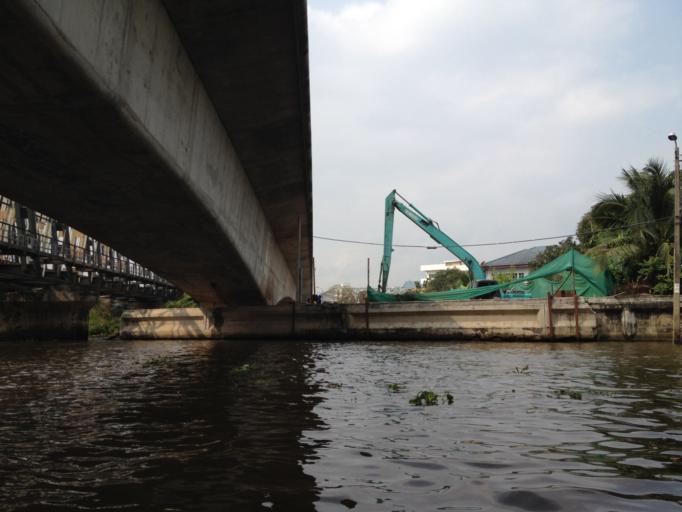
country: TH
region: Bangkok
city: Taling Chan
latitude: 13.7894
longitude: 100.4664
